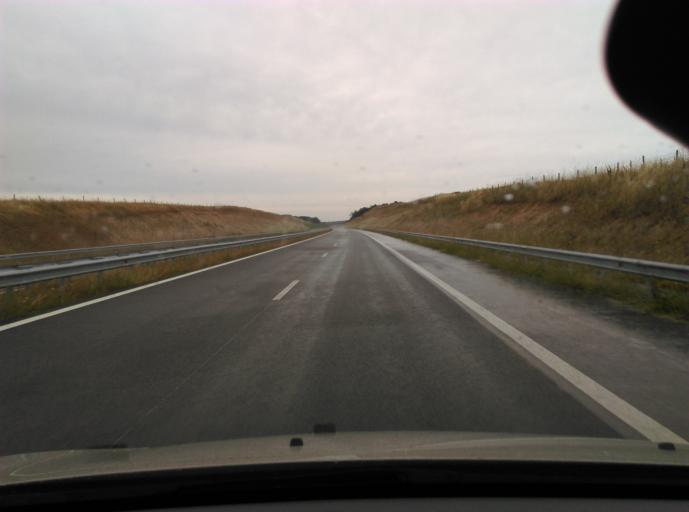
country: BG
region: Khaskovo
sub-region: Obshtina Dimitrovgrad
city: Dimitrovgrad
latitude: 42.0403
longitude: 25.5273
